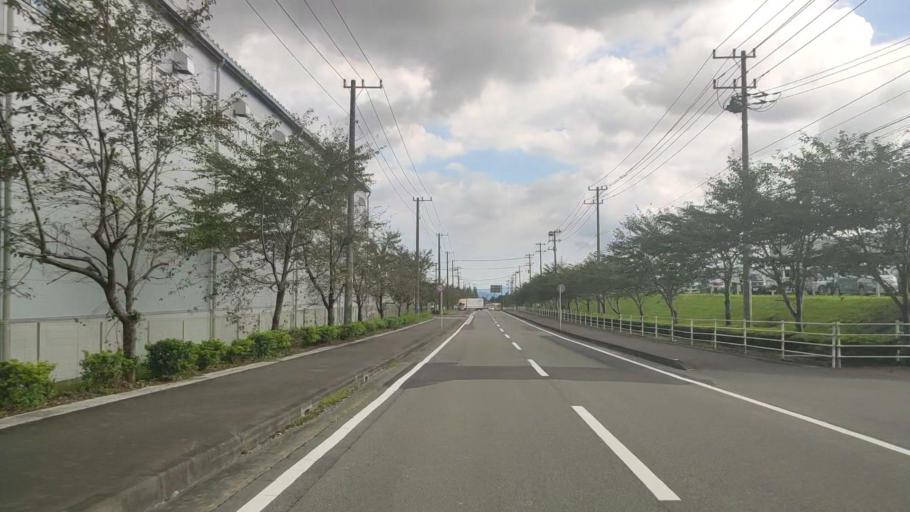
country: JP
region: Shizuoka
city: Gotemba
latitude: 35.2725
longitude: 138.8947
